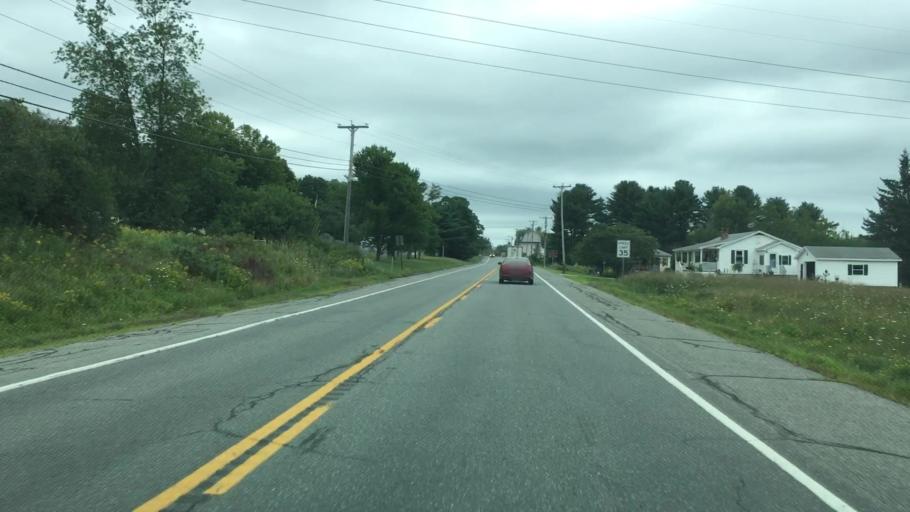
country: US
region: Maine
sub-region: Waldo County
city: Stockton Springs
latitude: 44.5496
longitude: -68.8643
